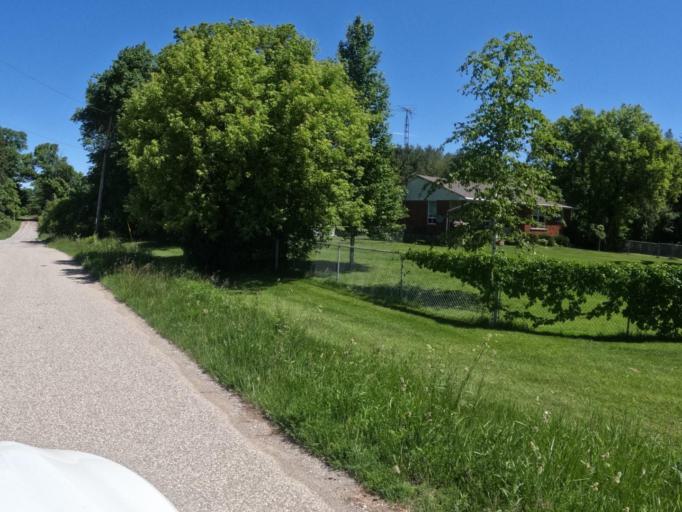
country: CA
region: Ontario
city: Norfolk County
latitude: 42.8665
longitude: -80.1771
